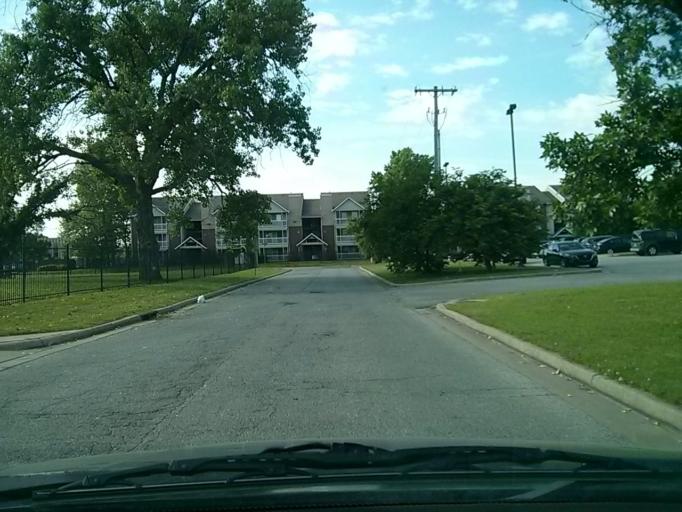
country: US
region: Oklahoma
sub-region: Tulsa County
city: Jenks
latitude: 36.0682
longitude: -95.9781
